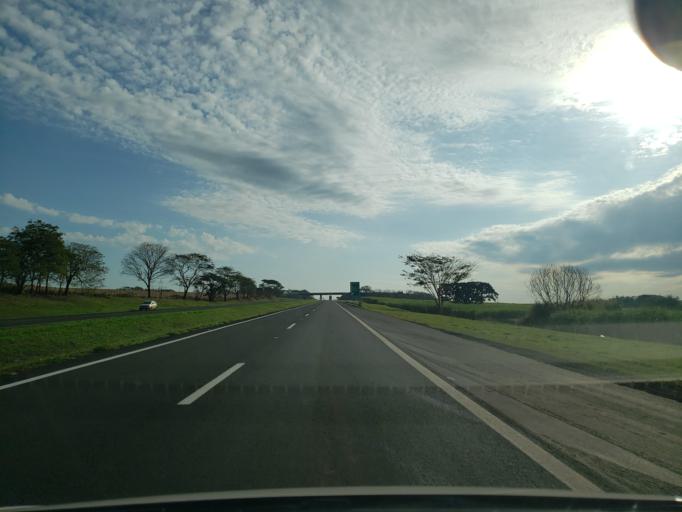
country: BR
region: Sao Paulo
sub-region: Valparaiso
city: Valparaiso
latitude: -21.2053
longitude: -50.7882
